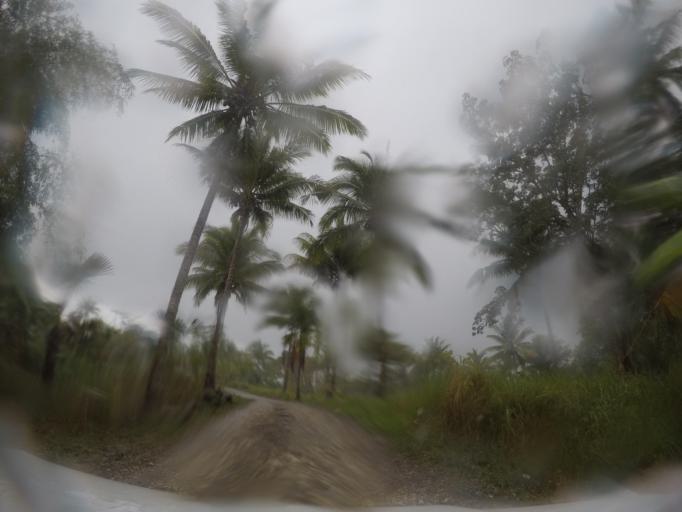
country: TL
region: Baucau
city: Venilale
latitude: -8.6319
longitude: 126.4432
